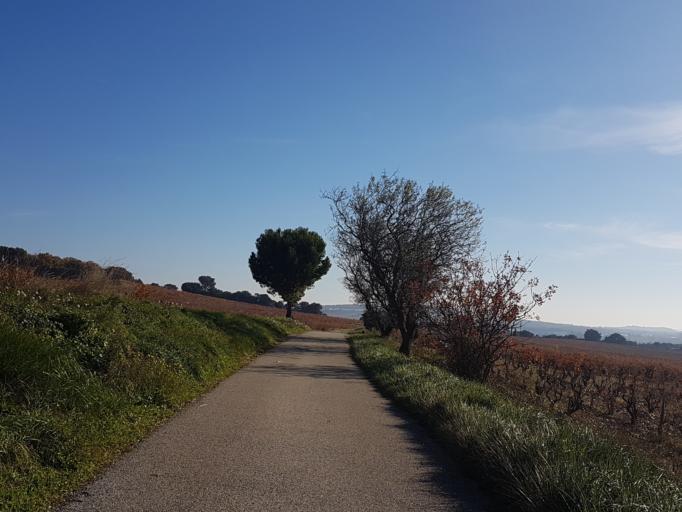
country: FR
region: Provence-Alpes-Cote d'Azur
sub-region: Departement du Vaucluse
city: Bedarrides
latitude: 44.0399
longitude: 4.8727
